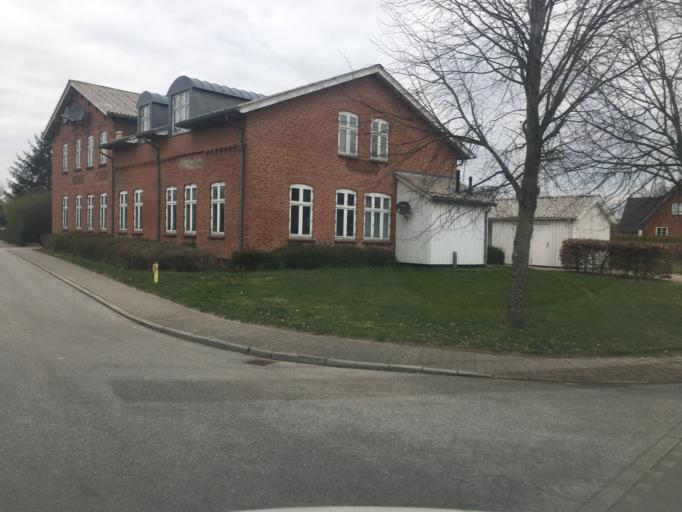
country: DK
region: South Denmark
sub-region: Tonder Kommune
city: Toftlund
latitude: 55.0610
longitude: 9.1063
